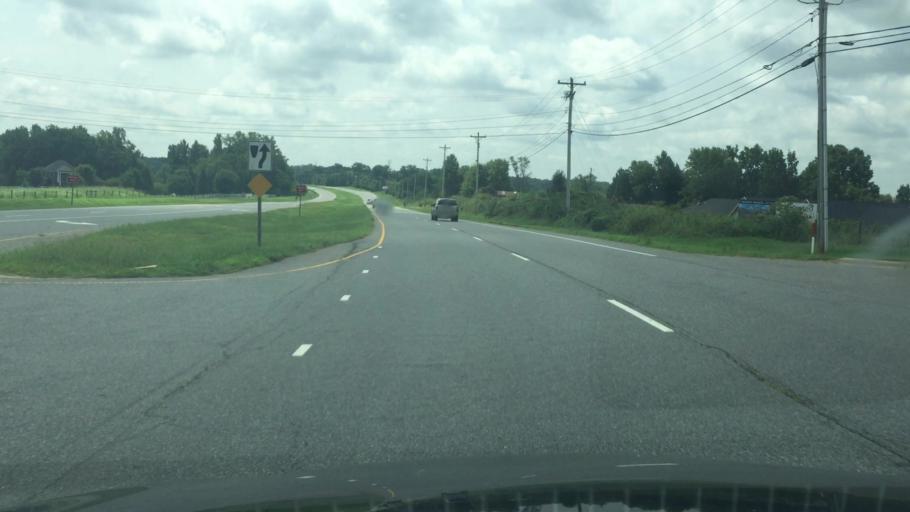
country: US
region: North Carolina
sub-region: Rowan County
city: Enochville
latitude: 35.4816
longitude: -80.6740
